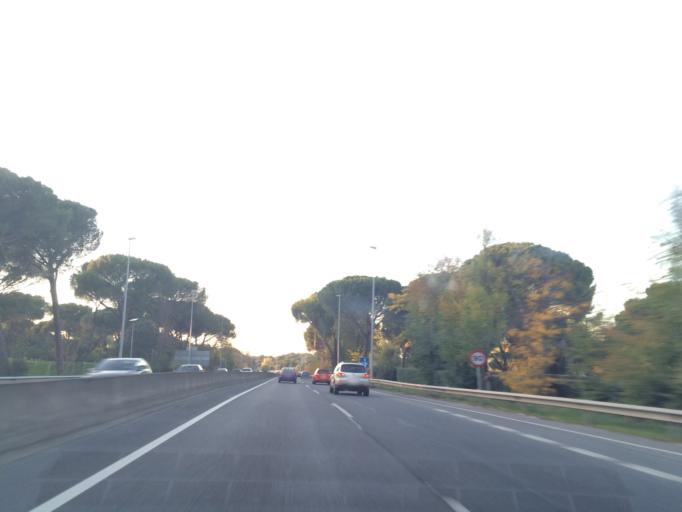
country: ES
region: Madrid
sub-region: Provincia de Madrid
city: Moncloa-Aravaca
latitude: 40.4396
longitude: -3.7440
